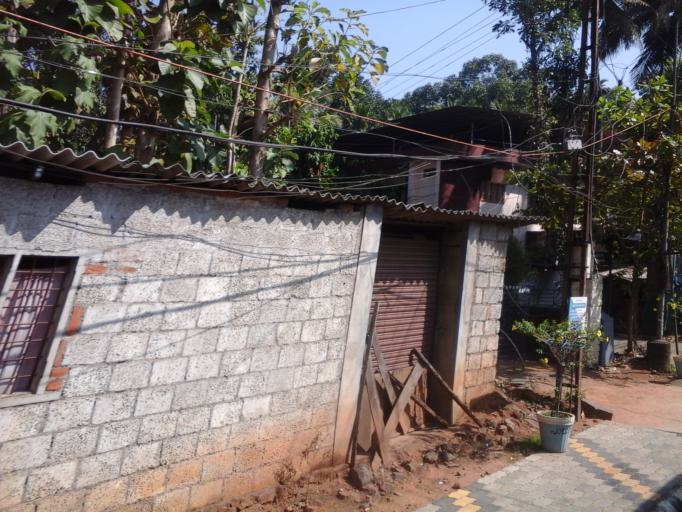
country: IN
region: Kerala
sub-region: Kottayam
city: Lalam
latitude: 9.7120
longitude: 76.7020
